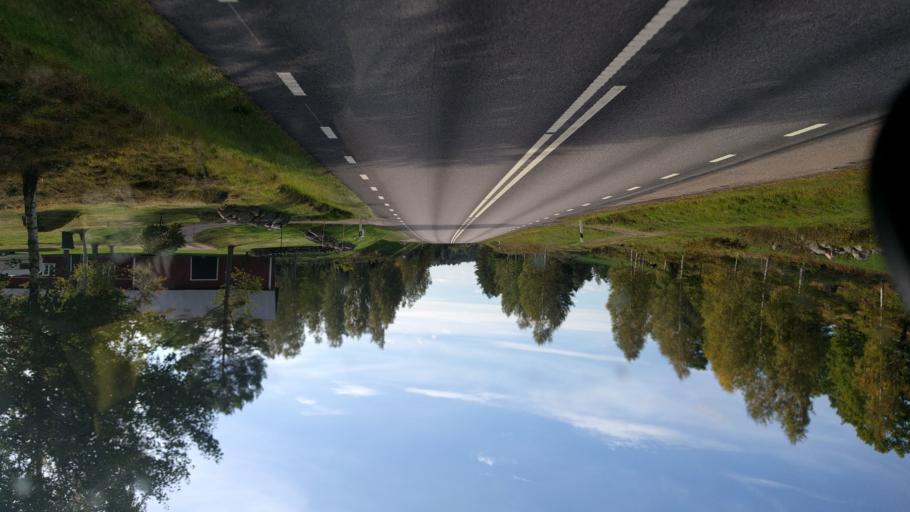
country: SE
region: OEstergoetland
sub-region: Kinda Kommun
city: Kisa
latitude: 57.9199
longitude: 15.6797
